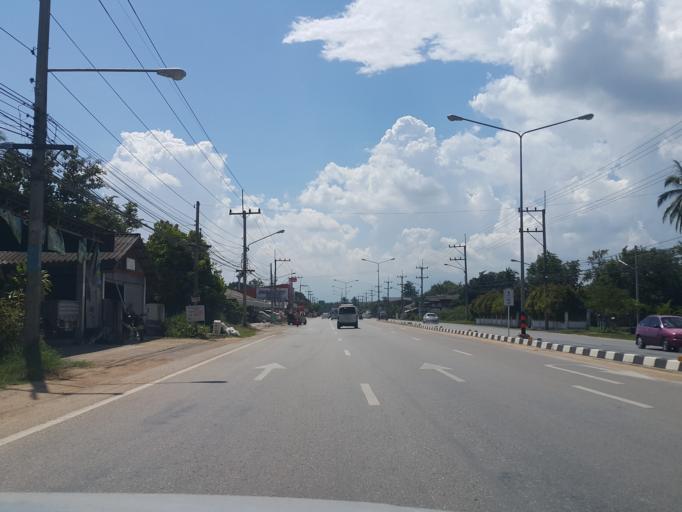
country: TH
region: Chiang Mai
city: Mae Taeng
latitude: 19.0351
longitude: 98.9464
